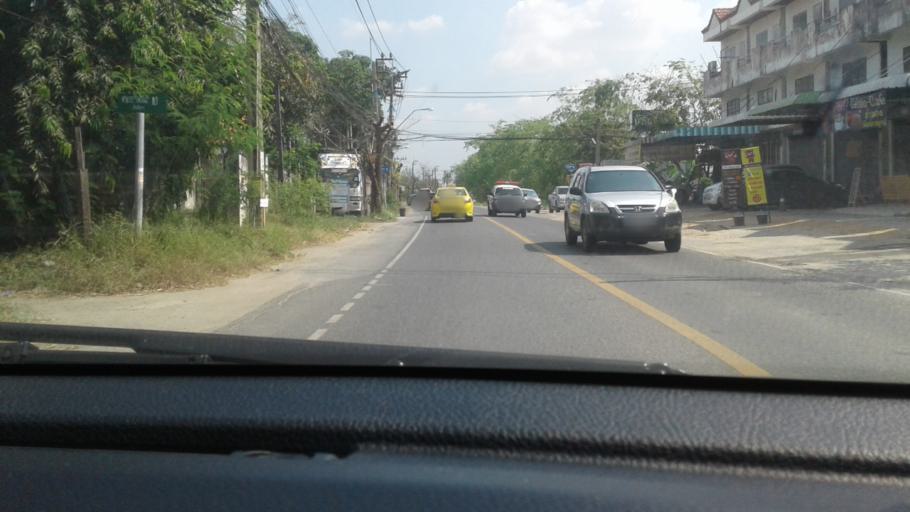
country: TH
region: Nonthaburi
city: Bang Yai
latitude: 13.7972
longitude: 100.3864
